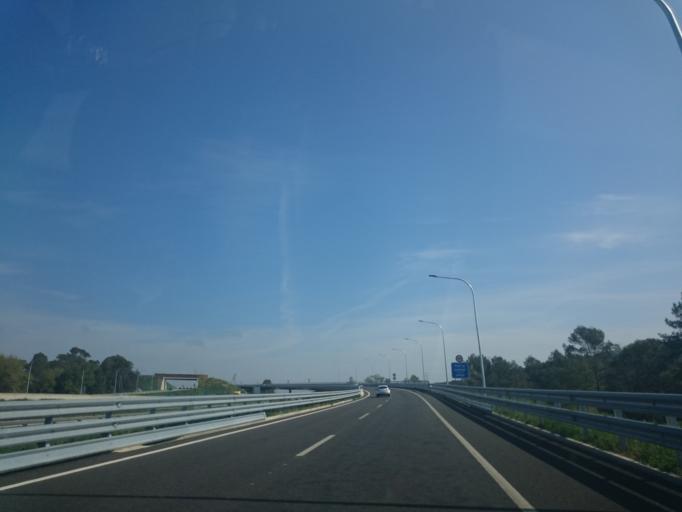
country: ES
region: Catalonia
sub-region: Provincia de Girona
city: Cervia de Ter
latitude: 42.0735
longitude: 2.8881
